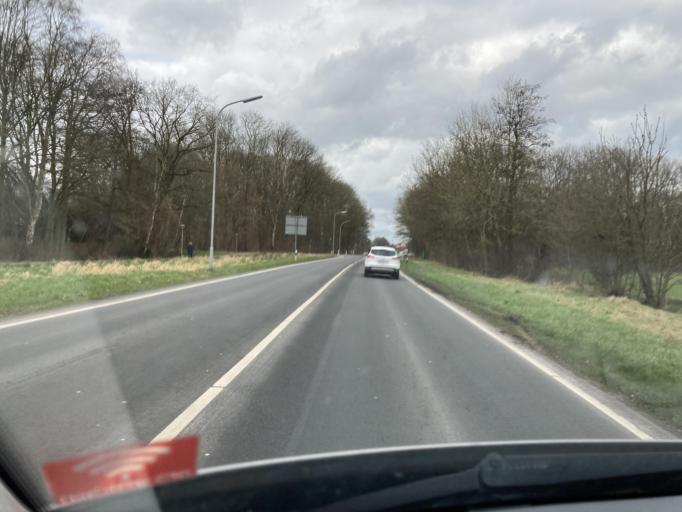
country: DE
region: Lower Saxony
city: Wilhelmshaven
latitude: 53.5414
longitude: 8.0868
